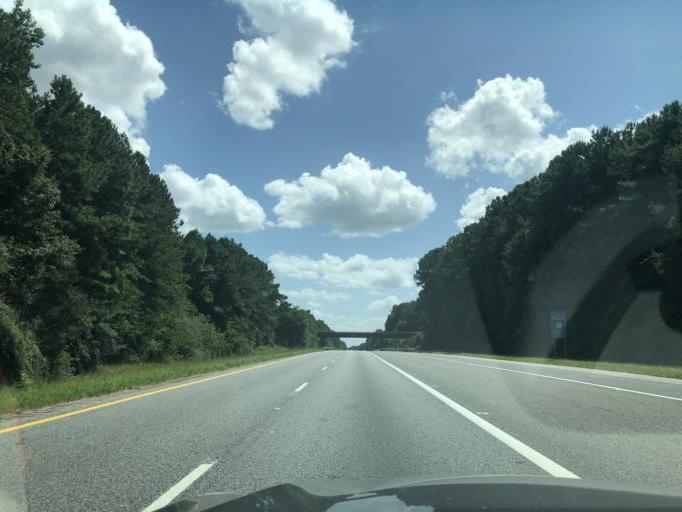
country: US
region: Georgia
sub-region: Troup County
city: La Grange
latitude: 33.0446
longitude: -84.9504
